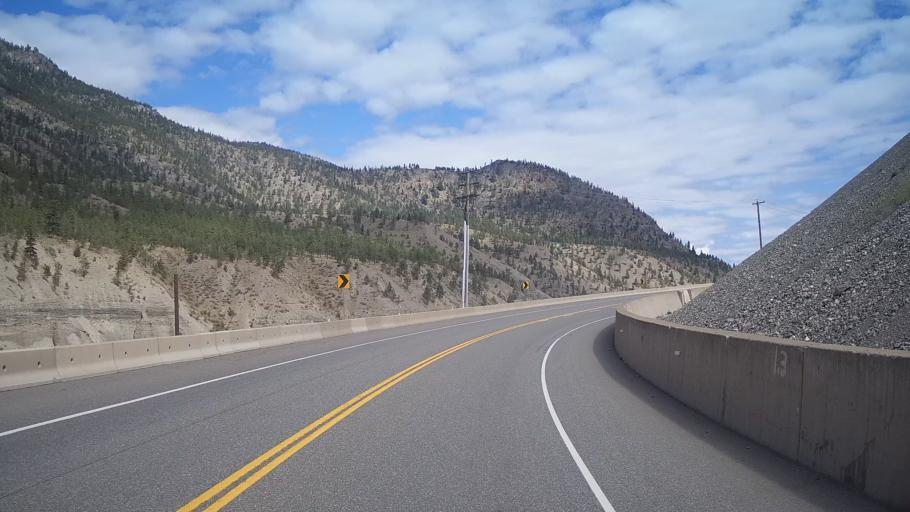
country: CA
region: British Columbia
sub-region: Thompson-Nicola Regional District
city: Ashcroft
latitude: 50.2792
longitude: -121.4060
